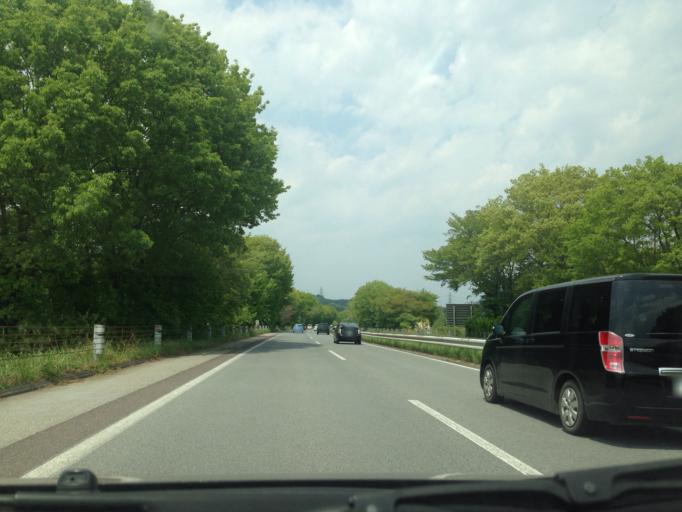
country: JP
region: Tochigi
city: Utsunomiya-shi
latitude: 36.6444
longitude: 139.8404
